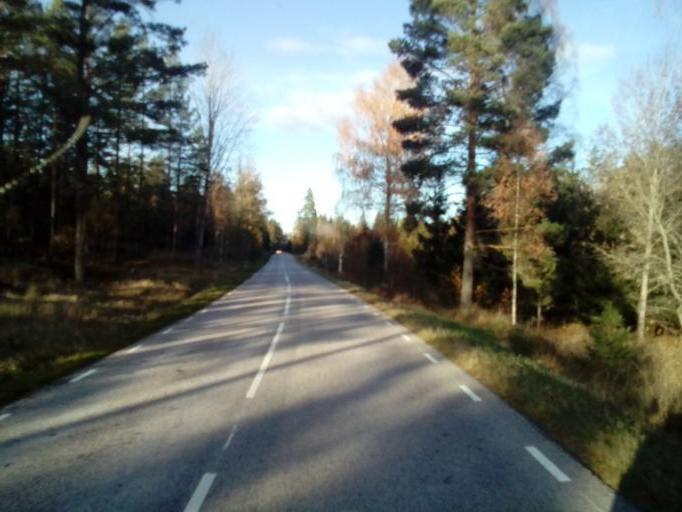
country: SE
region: Kalmar
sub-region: Vasterviks Kommun
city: Ankarsrum
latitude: 57.7628
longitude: 16.1357
